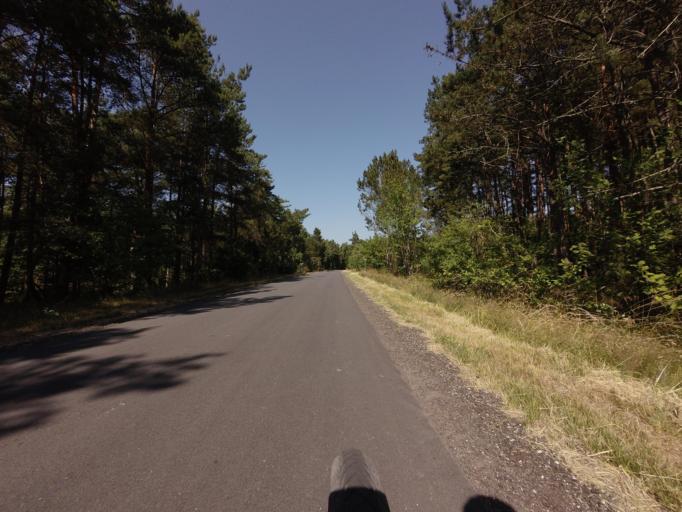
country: DK
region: North Denmark
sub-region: Laeso Kommune
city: Byrum
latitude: 57.2633
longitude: 11.0012
